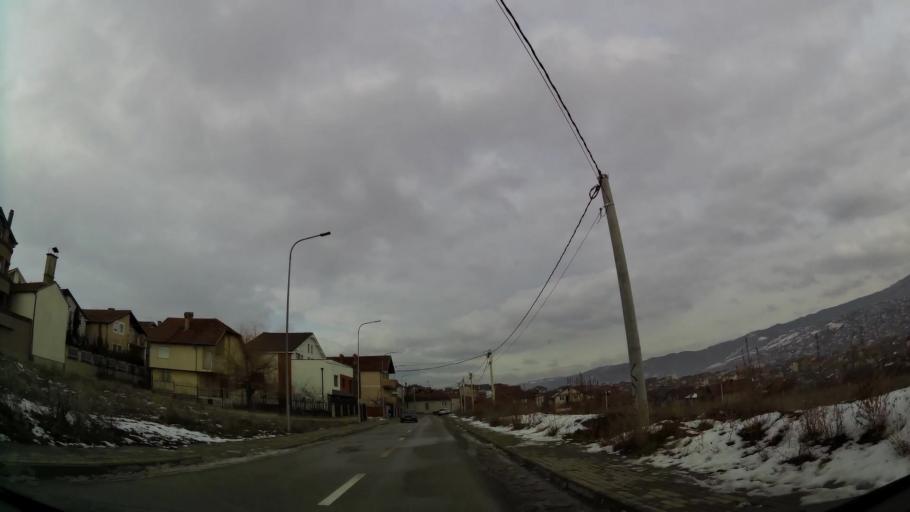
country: XK
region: Pristina
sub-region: Komuna e Prishtines
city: Pristina
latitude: 42.6727
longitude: 21.1546
